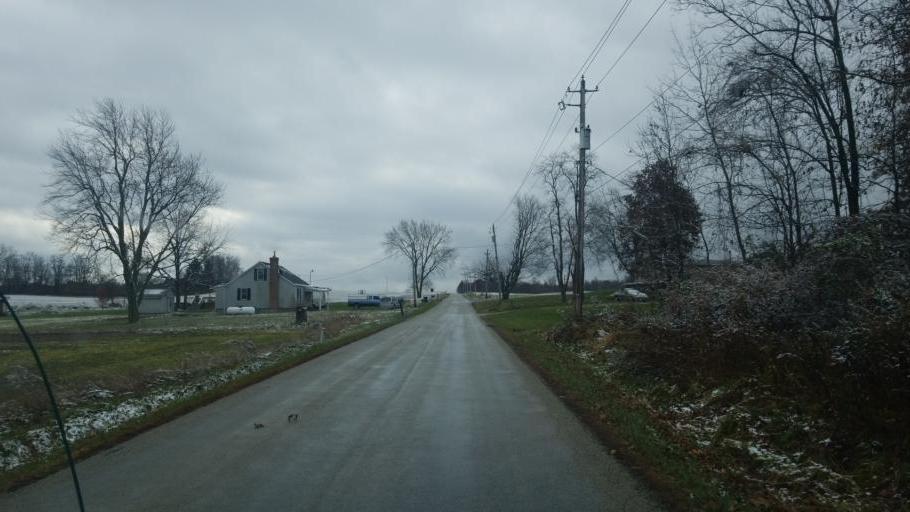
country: US
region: Ohio
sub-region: Richland County
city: Ontario
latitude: 40.8446
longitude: -82.5522
